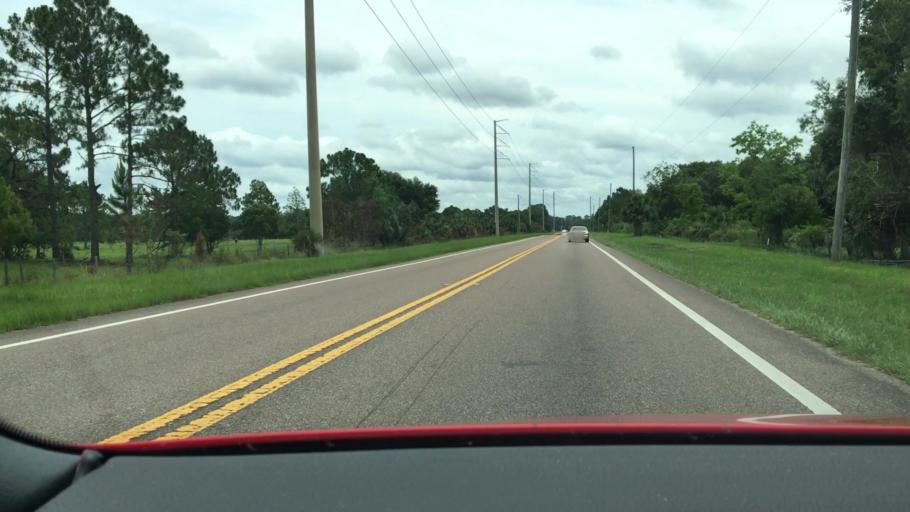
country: US
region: Florida
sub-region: Lake County
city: Eustis
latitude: 28.8753
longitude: -81.6786
